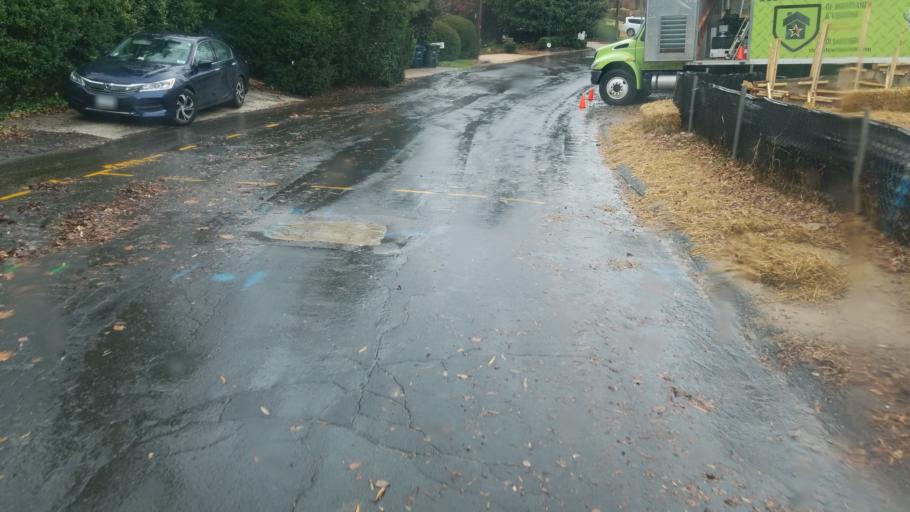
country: US
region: Maryland
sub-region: Montgomery County
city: Brookmont
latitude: 38.9278
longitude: -77.0979
